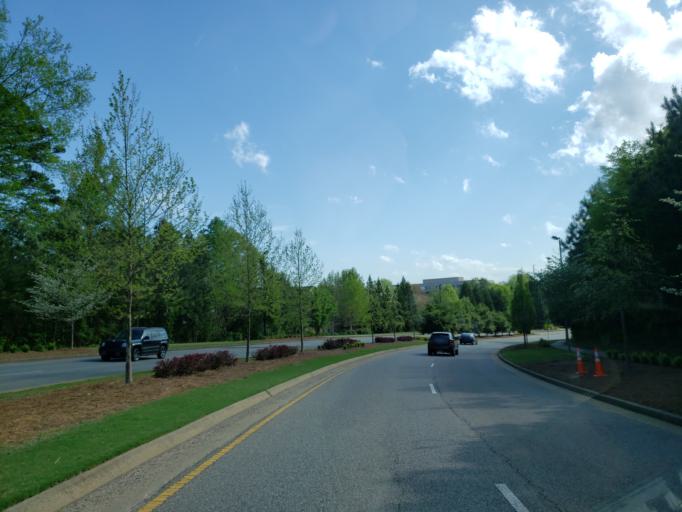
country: US
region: Georgia
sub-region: Fulton County
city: Alpharetta
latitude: 34.0640
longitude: -84.2838
